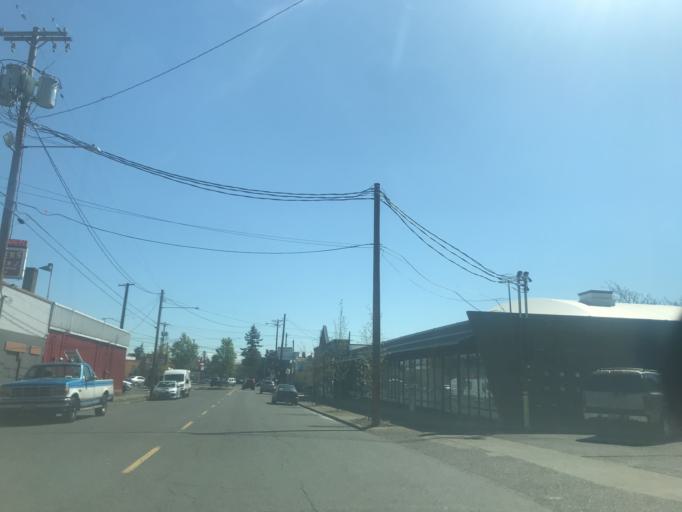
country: US
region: Oregon
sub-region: Multnomah County
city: Lents
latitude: 45.4831
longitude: -122.5812
